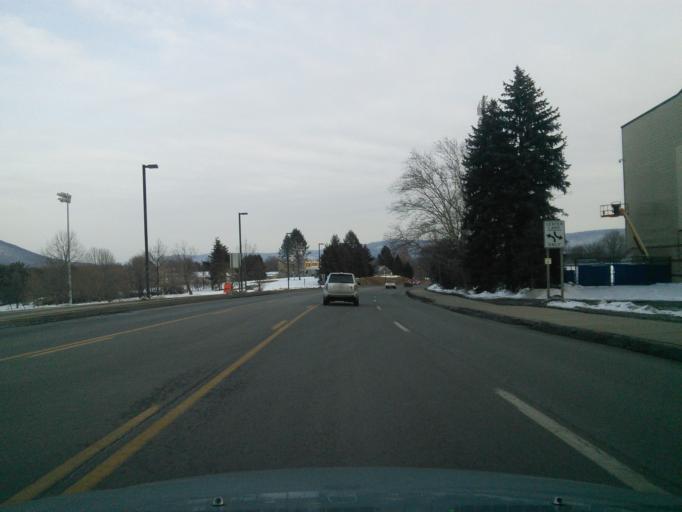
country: US
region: Pennsylvania
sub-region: Centre County
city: State College
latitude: 40.8068
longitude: -77.8549
